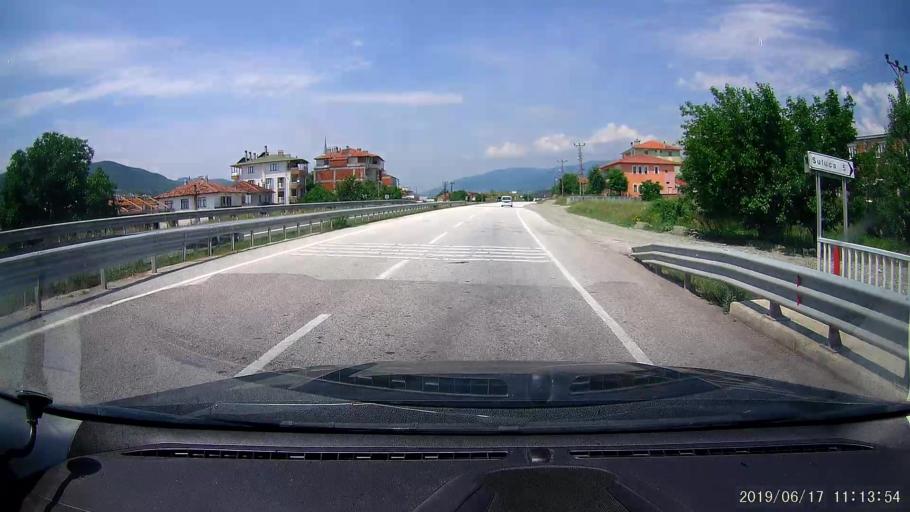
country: TR
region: Kastamonu
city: Tosya
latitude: 40.9562
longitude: 33.9619
